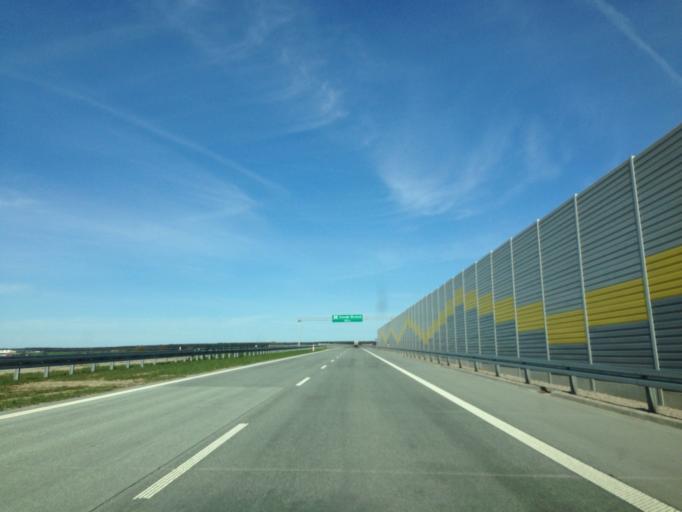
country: PL
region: Lodz Voivodeship
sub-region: Powiat sieradzki
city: Sieradz
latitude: 51.5793
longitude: 18.7972
